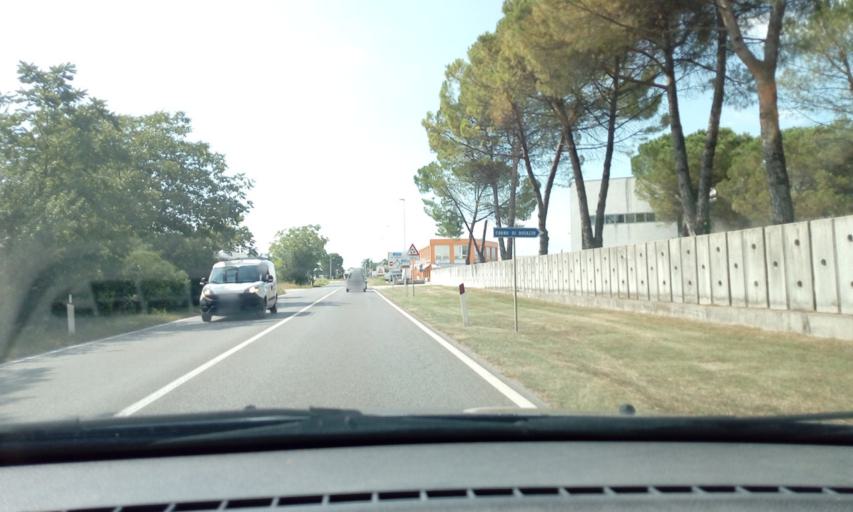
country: IT
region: Friuli Venezia Giulia
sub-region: Provincia di Udine
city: San Giovanni al Natisone
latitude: 45.9694
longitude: 13.4044
